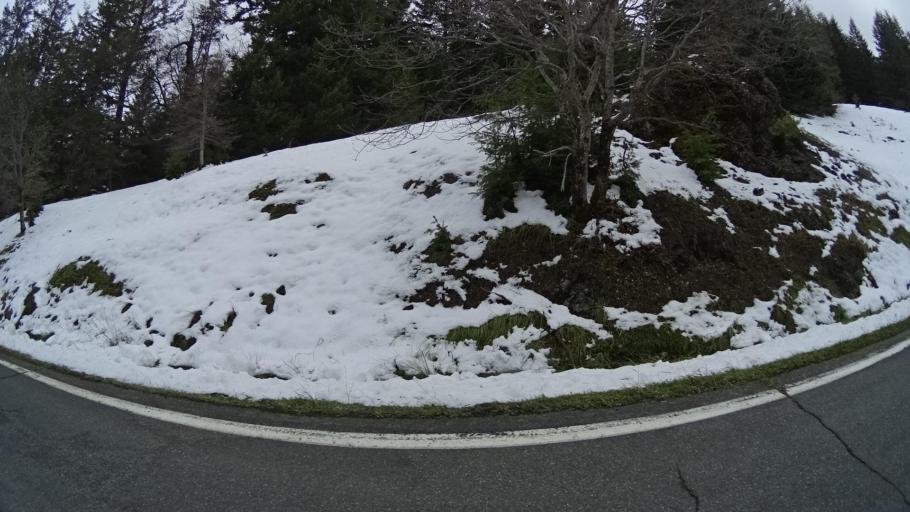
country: US
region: California
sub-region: Humboldt County
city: Willow Creek
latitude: 40.8746
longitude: -123.7545
